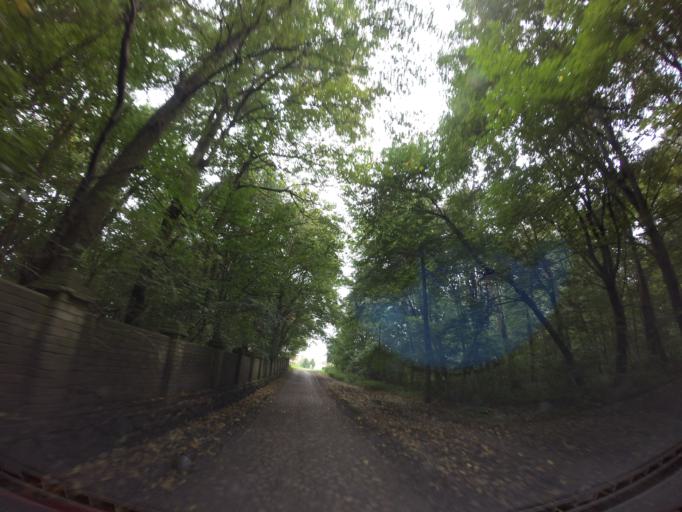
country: PL
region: West Pomeranian Voivodeship
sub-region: Powiat choszczenski
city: Krzecin
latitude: 53.0318
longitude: 15.4559
